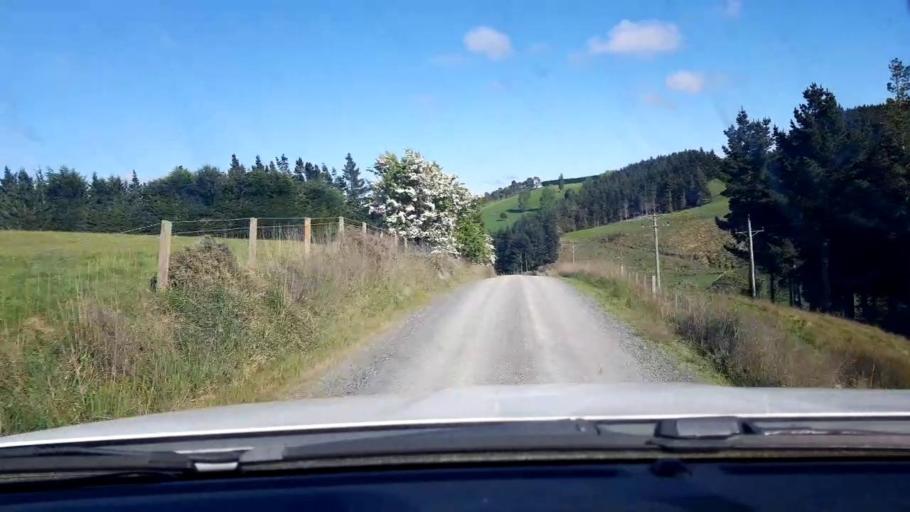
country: NZ
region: Otago
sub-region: Clutha District
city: Balclutha
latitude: -46.2234
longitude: 169.7446
